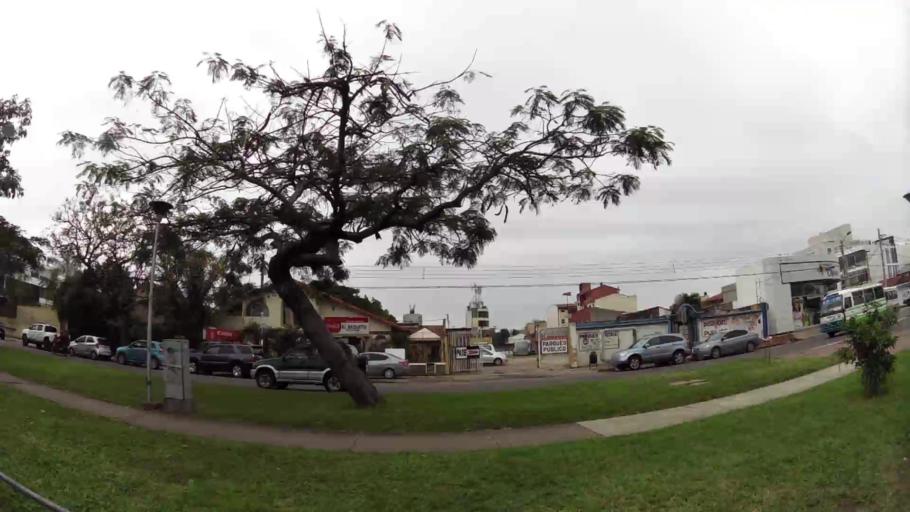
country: BO
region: Santa Cruz
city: Santa Cruz de la Sierra
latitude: -17.7860
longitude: -63.1718
